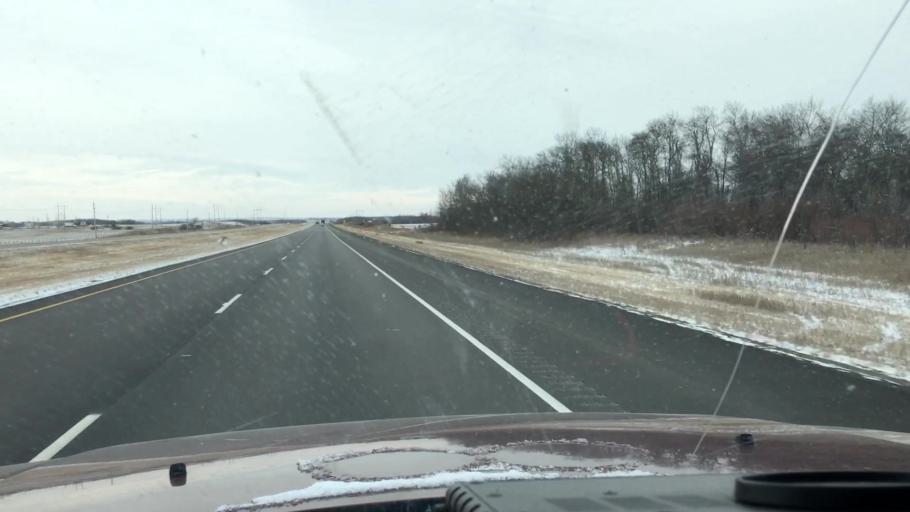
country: CA
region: Saskatchewan
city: Saskatoon
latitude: 51.9004
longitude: -106.5215
